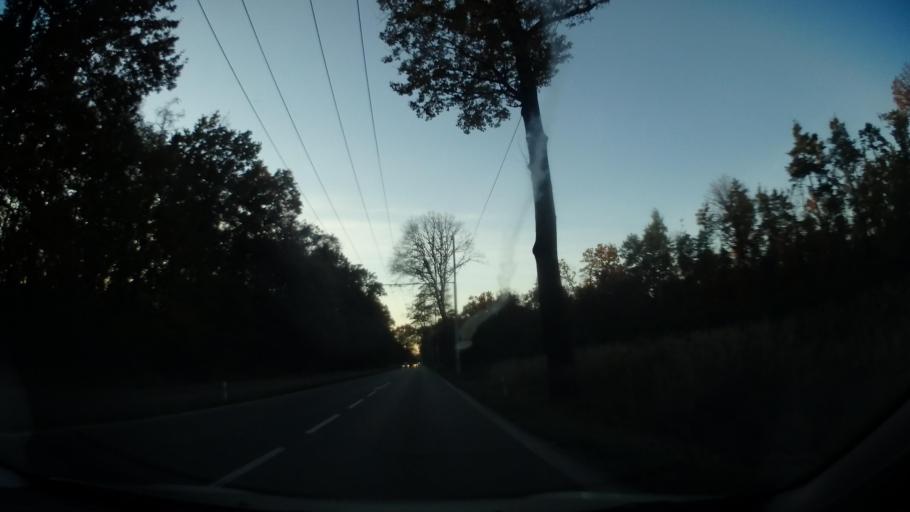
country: CZ
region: Pardubicky
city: Rybitvi
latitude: 50.0677
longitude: 15.7017
